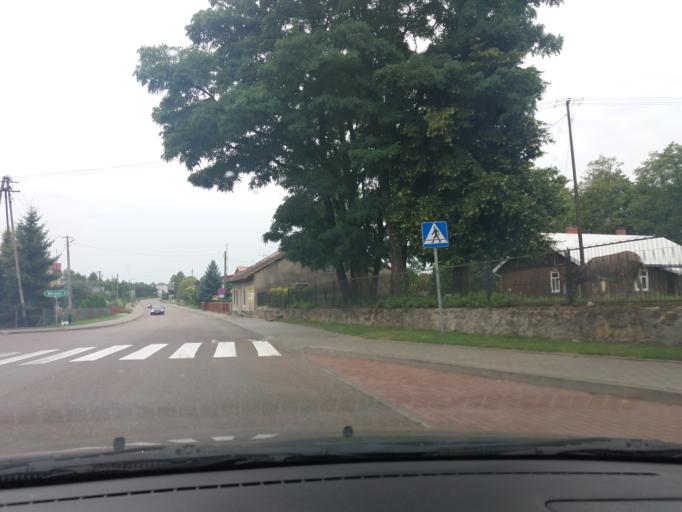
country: PL
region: Masovian Voivodeship
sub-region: Powiat mlawski
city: Wieczfnia Koscielna
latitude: 53.1950
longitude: 20.4757
